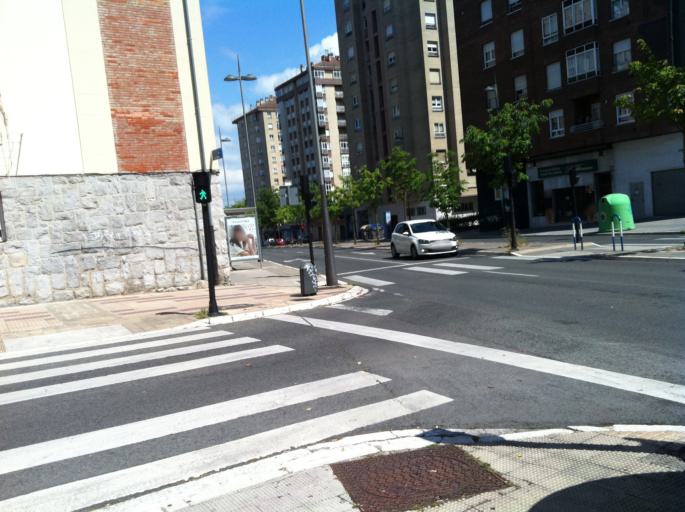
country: ES
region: Basque Country
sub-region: Provincia de Alava
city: Gasteiz / Vitoria
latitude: 42.8418
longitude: -2.6619
